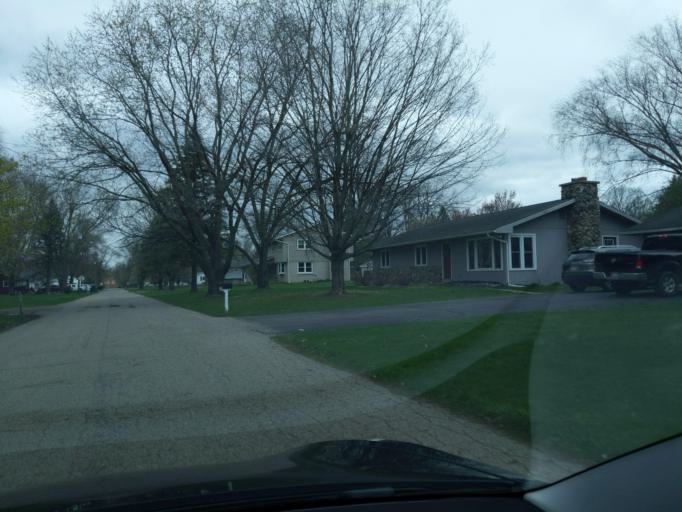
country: US
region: Michigan
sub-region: Ingham County
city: Stockbridge
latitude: 42.4448
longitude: -84.1824
